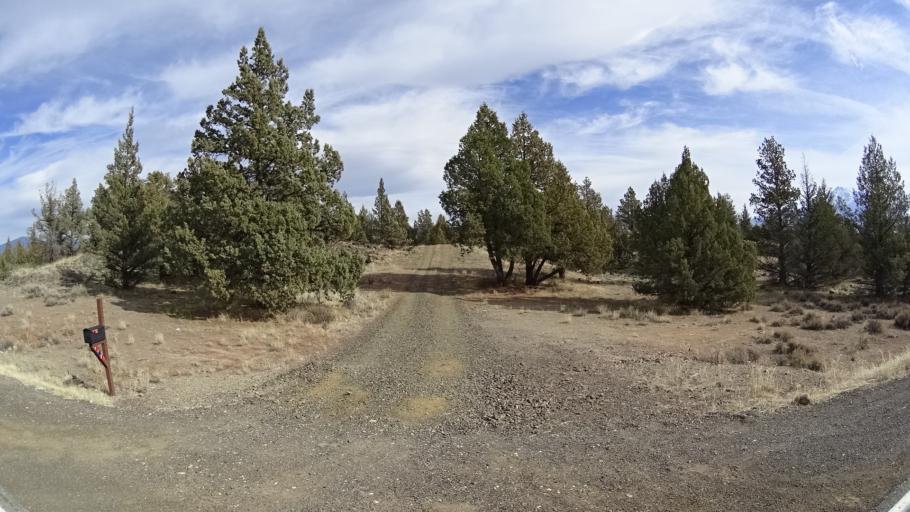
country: US
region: California
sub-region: Siskiyou County
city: Weed
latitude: 41.5890
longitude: -122.4001
